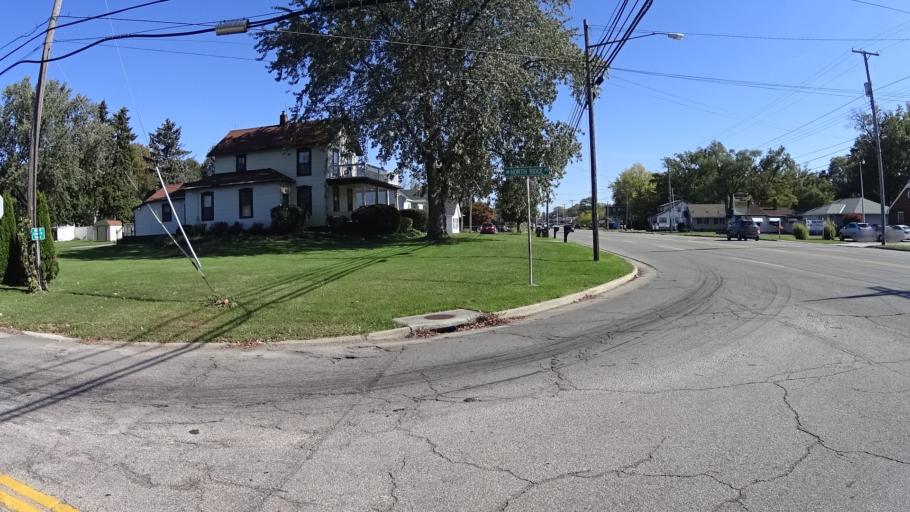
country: US
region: Ohio
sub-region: Lorain County
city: Lorain
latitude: 41.4183
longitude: -82.1585
